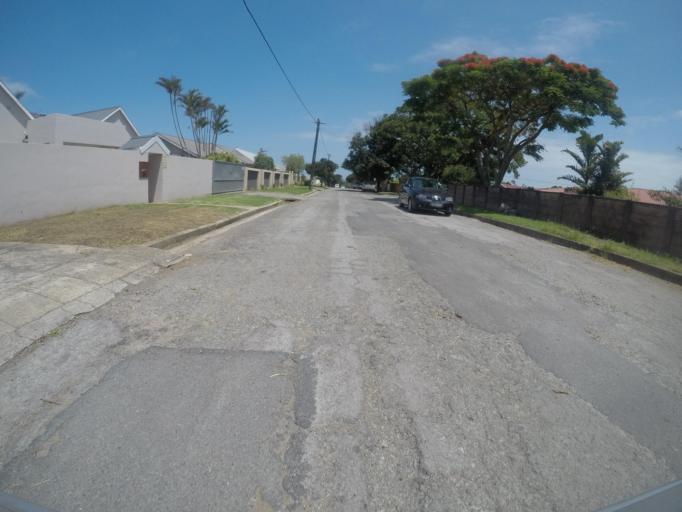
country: ZA
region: Eastern Cape
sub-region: Buffalo City Metropolitan Municipality
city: East London
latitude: -32.9744
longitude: 27.8799
